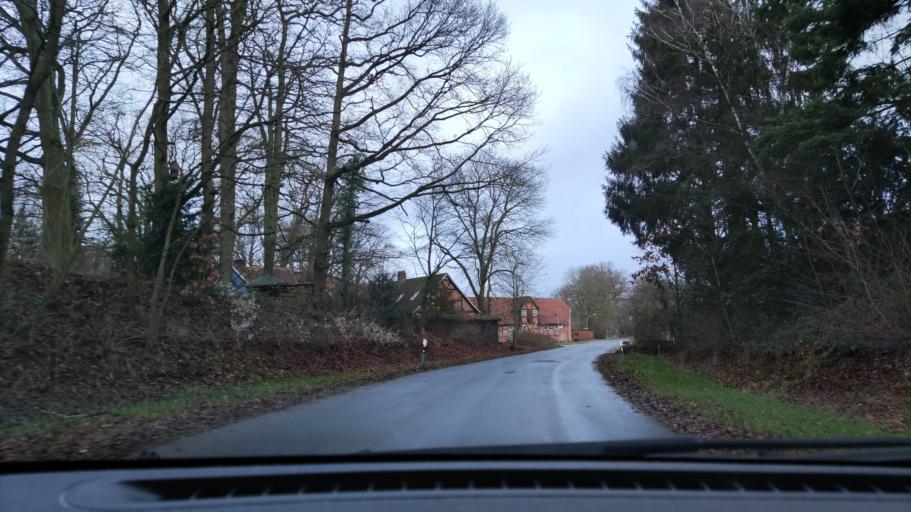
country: DE
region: Lower Saxony
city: Natendorf
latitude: 53.0939
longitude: 10.4405
